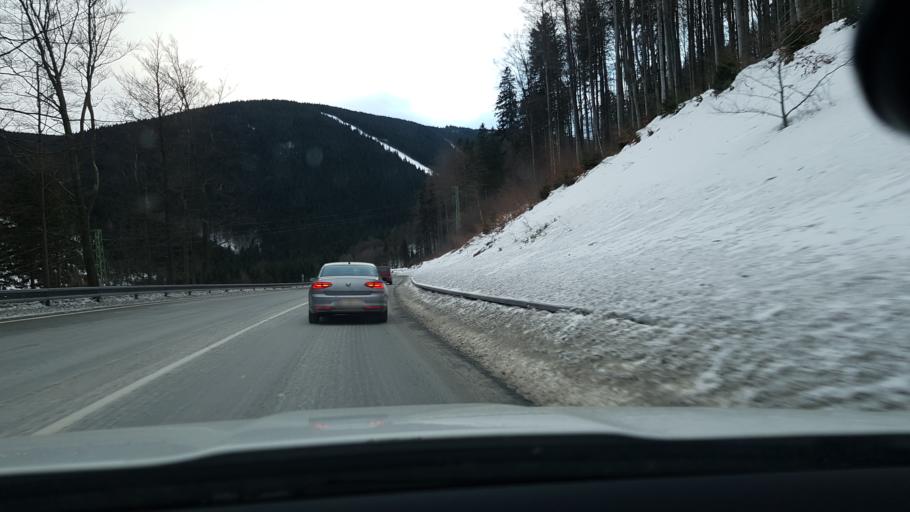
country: CZ
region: Olomoucky
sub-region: Okres Sumperk
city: Loucna nad Desnou
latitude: 50.1377
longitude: 17.1628
